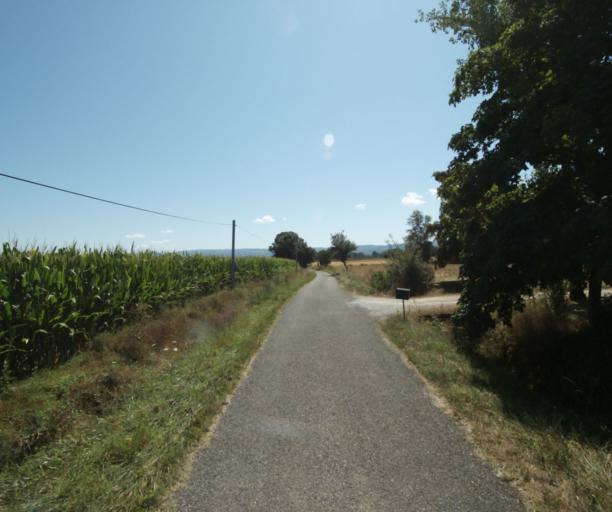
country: FR
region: Midi-Pyrenees
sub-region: Departement de la Haute-Garonne
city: Revel
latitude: 43.4888
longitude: 1.9588
